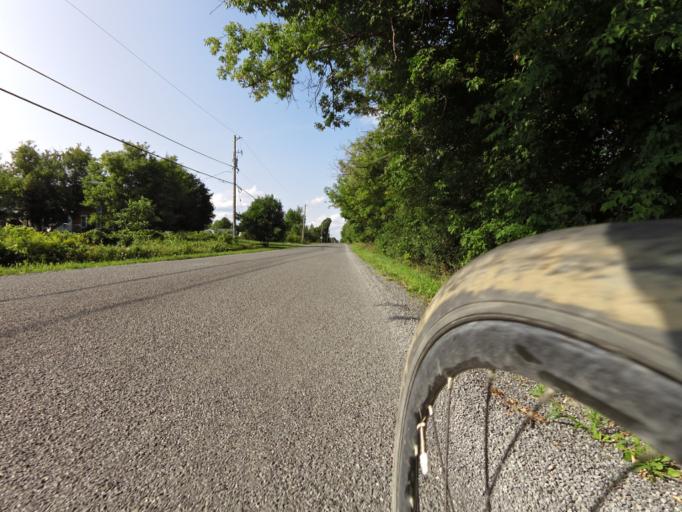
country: CA
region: Ontario
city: Kingston
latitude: 44.3829
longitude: -76.5956
